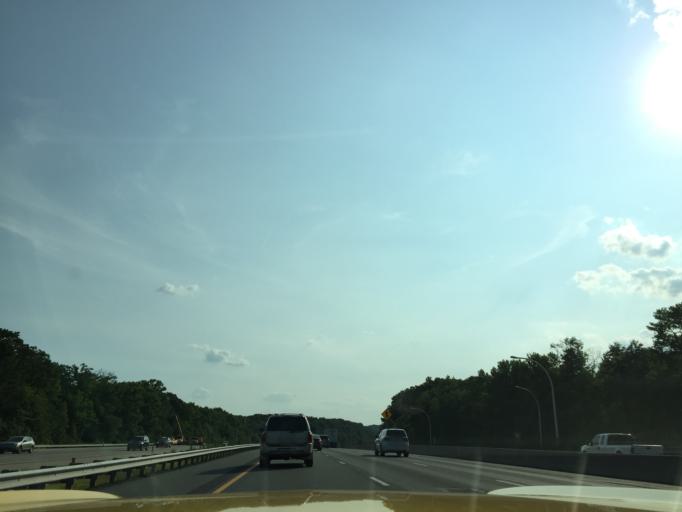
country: US
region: Maryland
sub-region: Cecil County
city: North East
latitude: 39.6305
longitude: -75.9599
